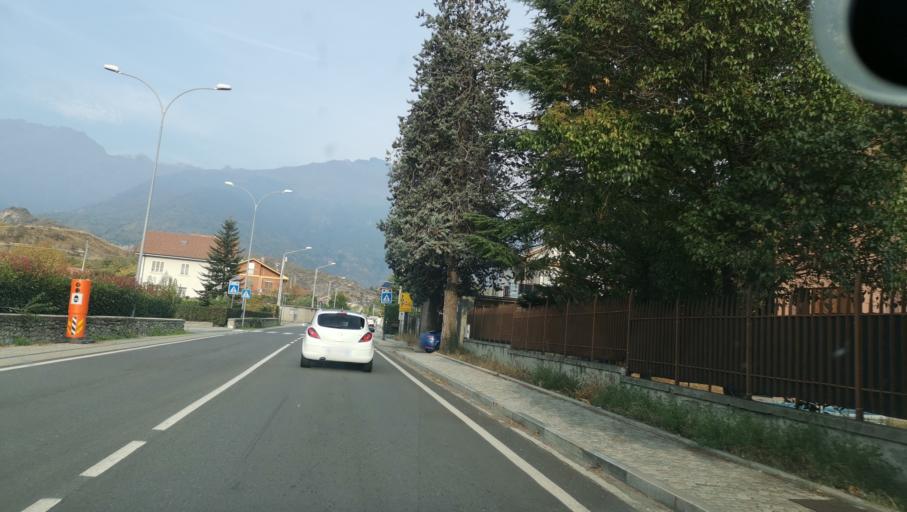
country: IT
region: Piedmont
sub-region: Provincia di Torino
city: Susa
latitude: 45.1348
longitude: 7.0589
